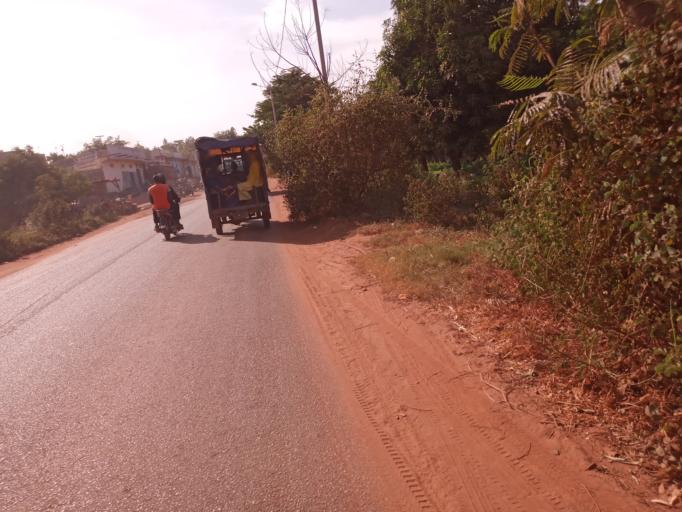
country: ML
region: Bamako
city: Bamako
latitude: 12.6291
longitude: -7.9479
